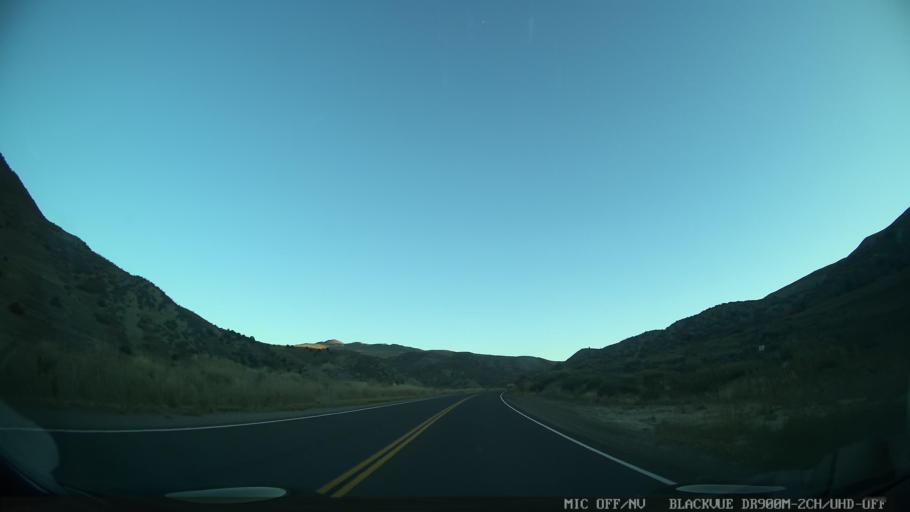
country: US
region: Colorado
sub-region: Eagle County
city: Edwards
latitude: 39.7913
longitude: -106.6795
